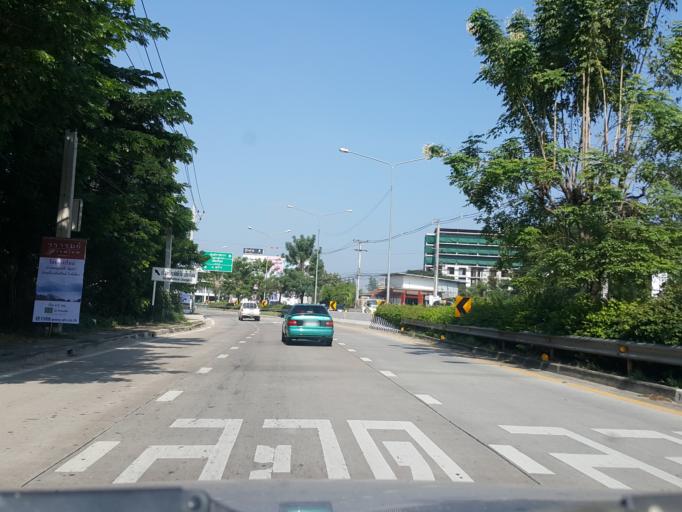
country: TH
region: Chiang Mai
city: San Sai
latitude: 18.8216
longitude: 99.0164
